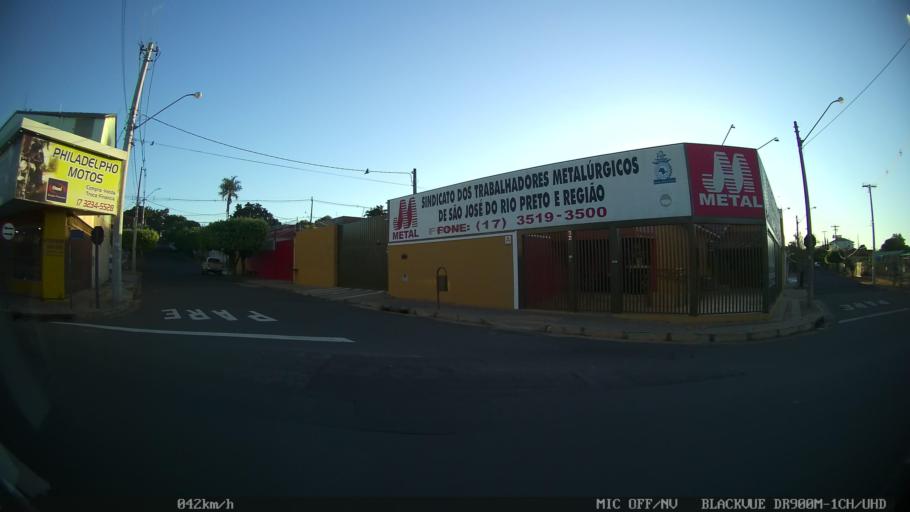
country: BR
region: Sao Paulo
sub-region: Sao Jose Do Rio Preto
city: Sao Jose do Rio Preto
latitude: -20.7910
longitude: -49.3771
